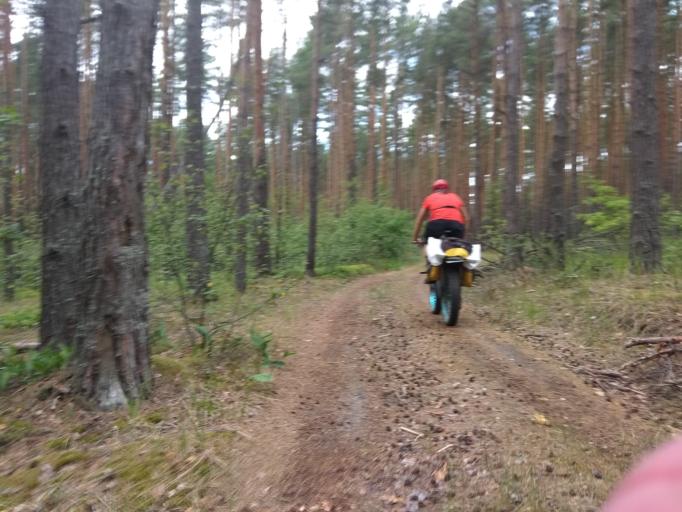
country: RU
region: Moskovskaya
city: Misheronskiy
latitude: 55.6381
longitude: 39.7156
